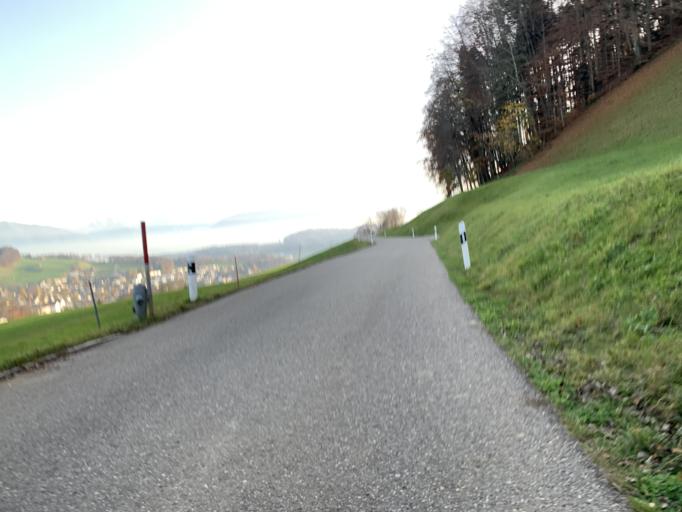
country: CH
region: Zurich
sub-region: Bezirk Hinwil
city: Wald
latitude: 47.2867
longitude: 8.9075
